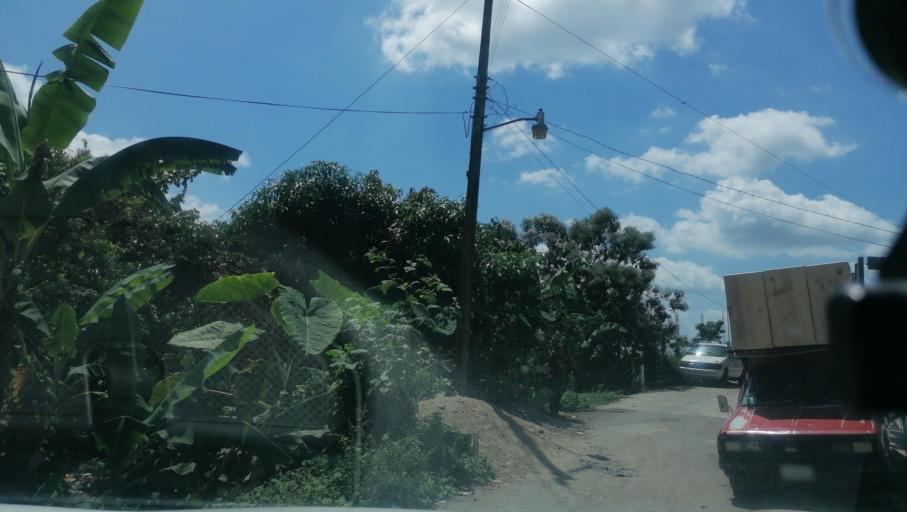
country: MX
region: Chiapas
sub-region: Cacahoatan
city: Benito Juarez
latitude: 15.0639
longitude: -92.1422
